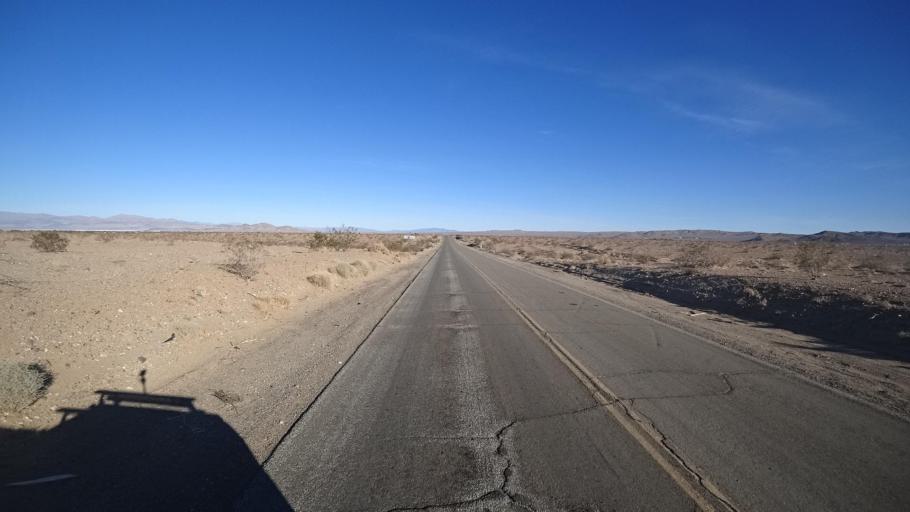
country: US
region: California
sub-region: Kern County
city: China Lake Acres
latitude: 35.6080
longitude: -117.7350
